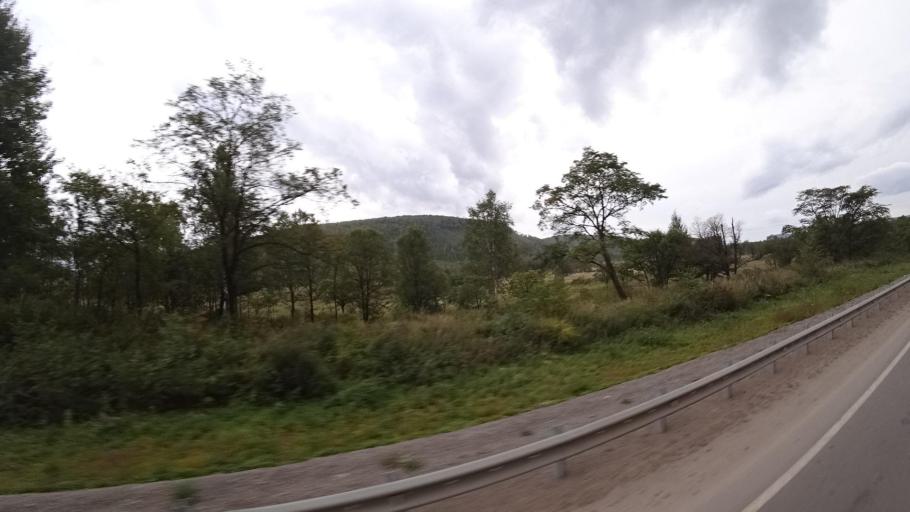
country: RU
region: Jewish Autonomous Oblast
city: Khingansk
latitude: 48.9911
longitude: 131.1168
